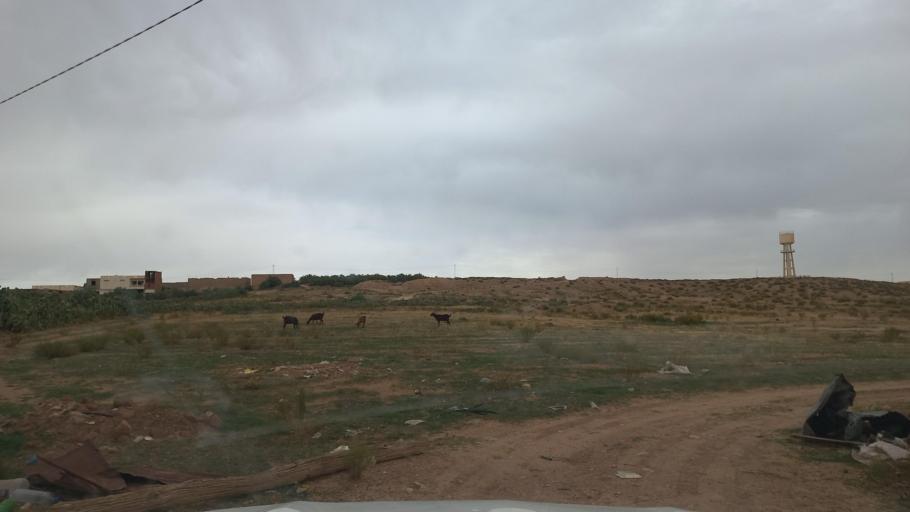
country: TN
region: Al Qasrayn
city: Sbiba
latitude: 35.3830
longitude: 9.0636
